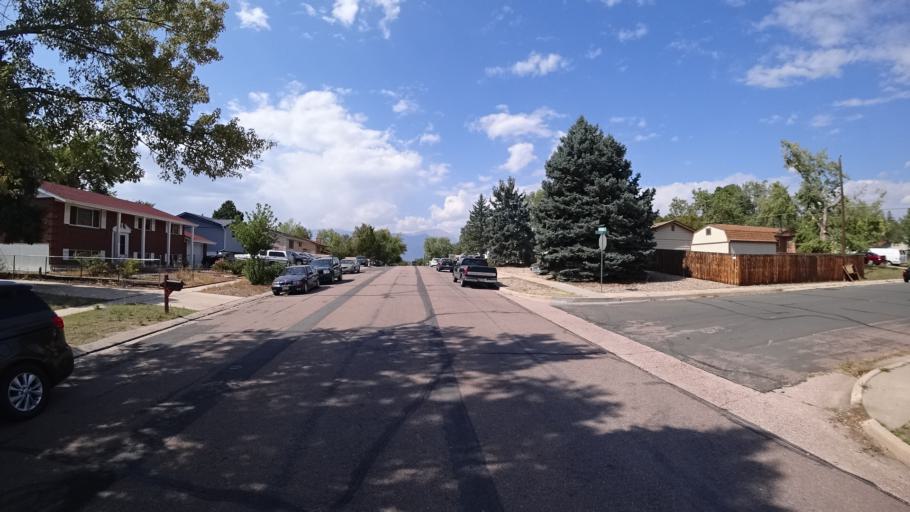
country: US
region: Colorado
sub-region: El Paso County
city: Colorado Springs
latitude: 38.8260
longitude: -104.7711
